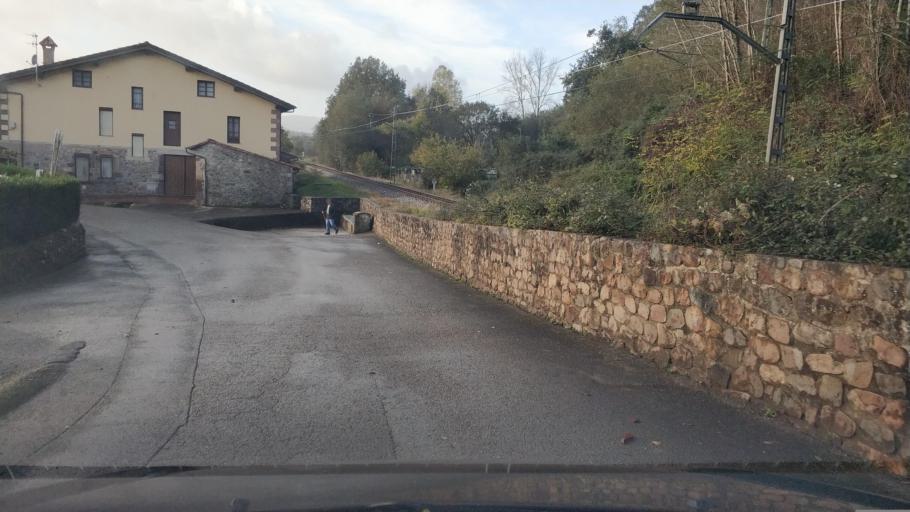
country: ES
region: Cantabria
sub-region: Provincia de Cantabria
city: Luzmela
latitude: 43.3374
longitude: -4.1801
